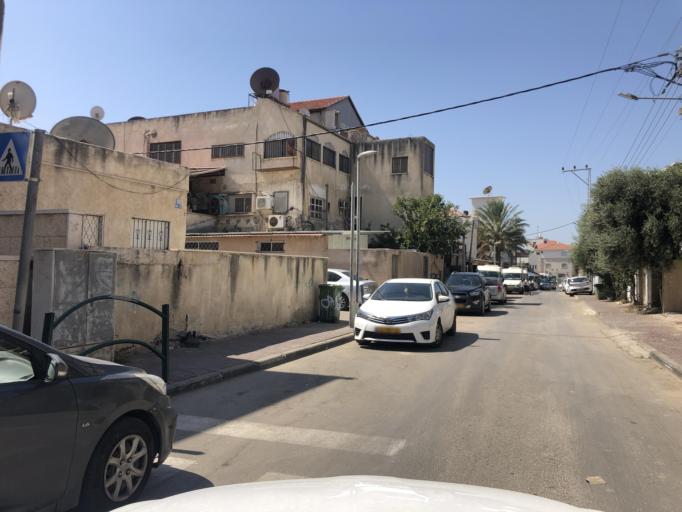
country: IL
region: Central District
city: Jaljulya
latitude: 32.1553
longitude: 34.9553
